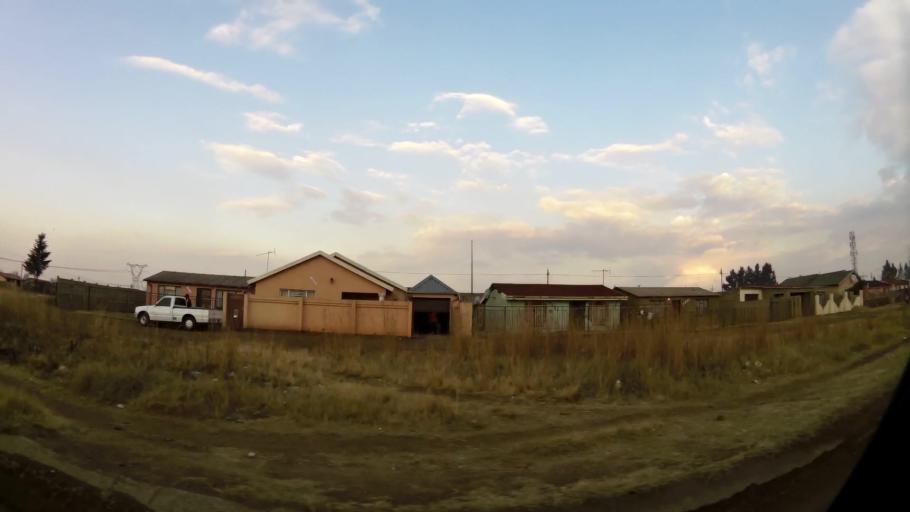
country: ZA
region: Gauteng
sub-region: City of Johannesburg Metropolitan Municipality
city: Orange Farm
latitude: -26.5580
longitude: 27.8387
